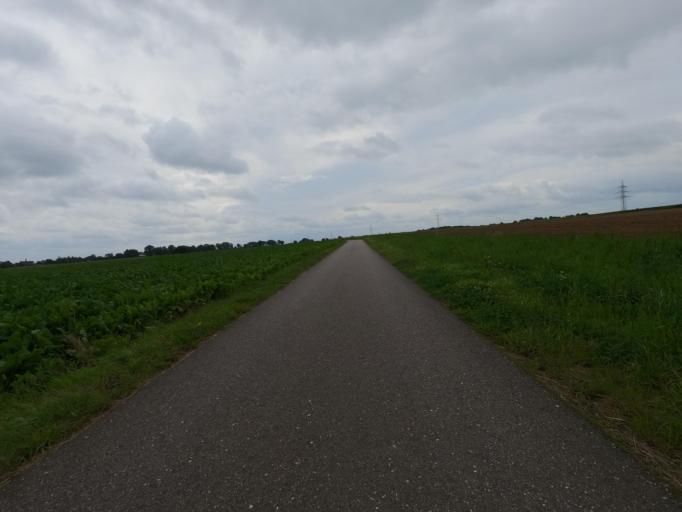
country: DE
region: North Rhine-Westphalia
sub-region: Regierungsbezirk Koln
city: Selfkant
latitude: 51.0104
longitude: 5.9547
